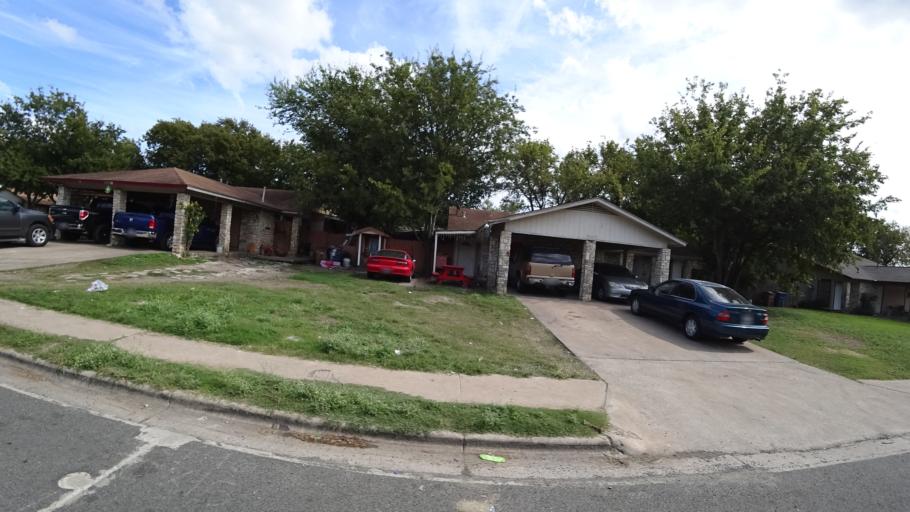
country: US
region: Texas
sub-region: Travis County
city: Austin
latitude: 30.1968
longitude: -97.7422
